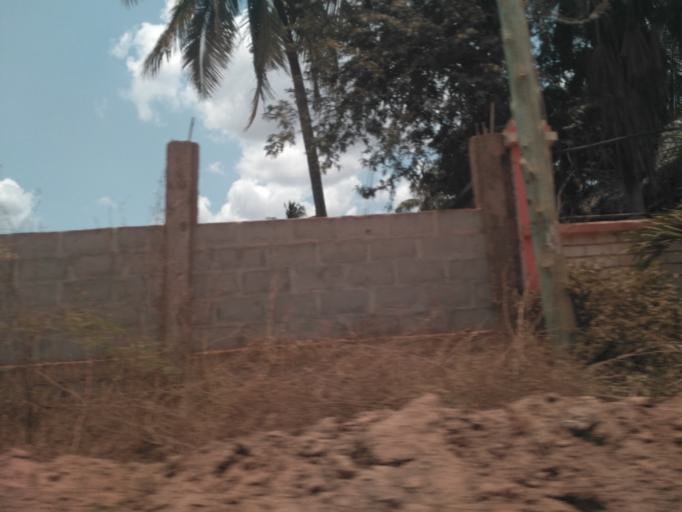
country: TZ
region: Dar es Salaam
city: Dar es Salaam
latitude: -6.8406
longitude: 39.3349
